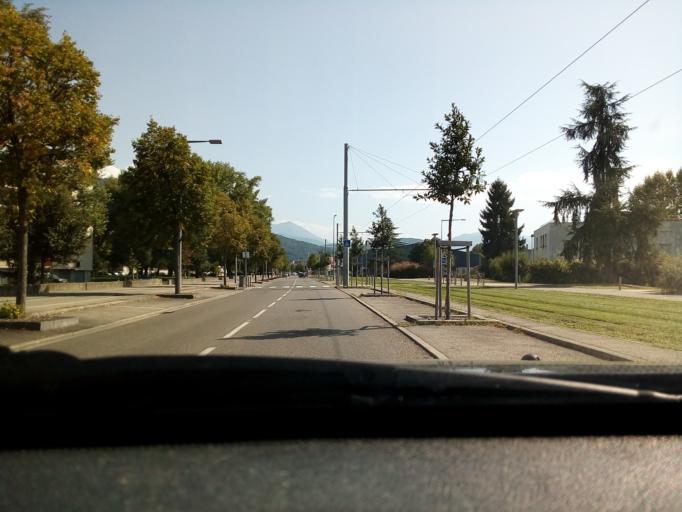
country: FR
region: Rhone-Alpes
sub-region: Departement de l'Isere
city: Saint-Martin-d'Heres
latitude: 45.1813
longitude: 5.7546
